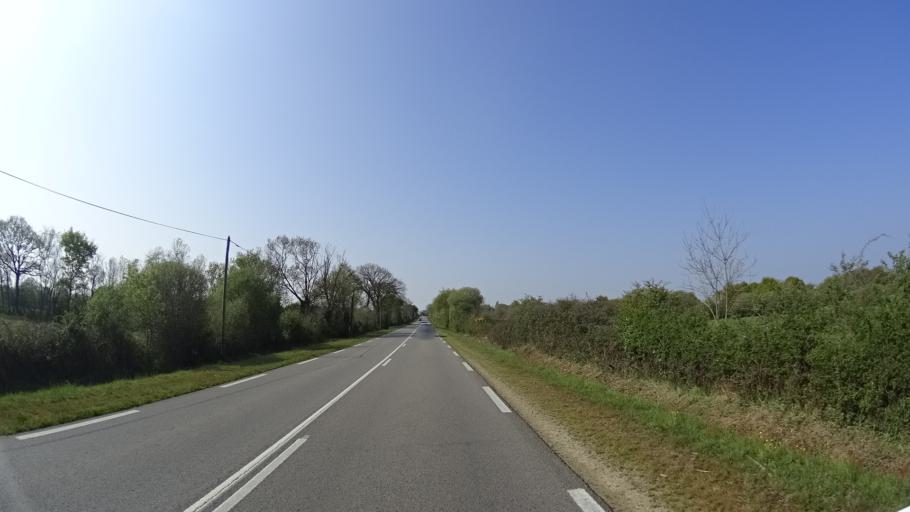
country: FR
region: Pays de la Loire
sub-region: Departement de la Loire-Atlantique
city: Bourgneuf-en-Retz
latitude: 47.0629
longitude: -1.9164
